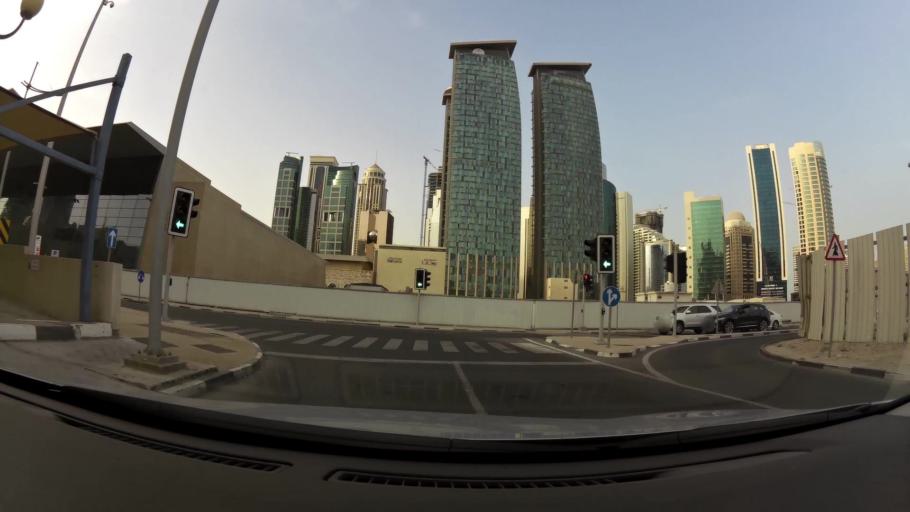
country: QA
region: Baladiyat ad Dawhah
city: Doha
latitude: 25.3219
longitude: 51.5328
